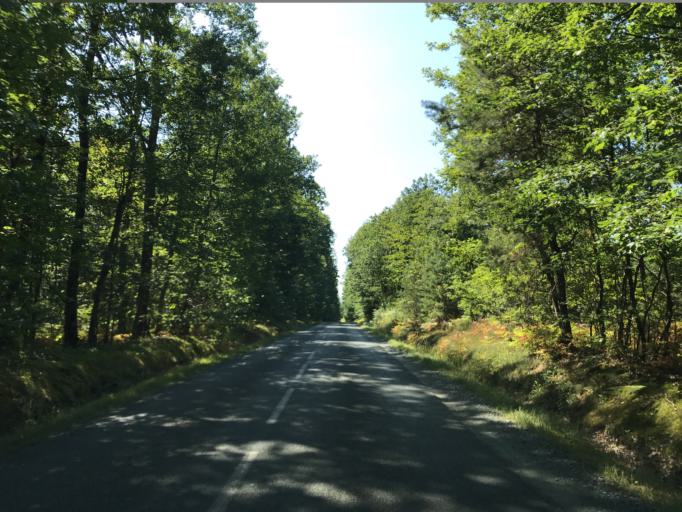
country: FR
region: Haute-Normandie
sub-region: Departement de l'Eure
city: Houlbec-Cocherel
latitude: 49.0868
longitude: 1.3269
